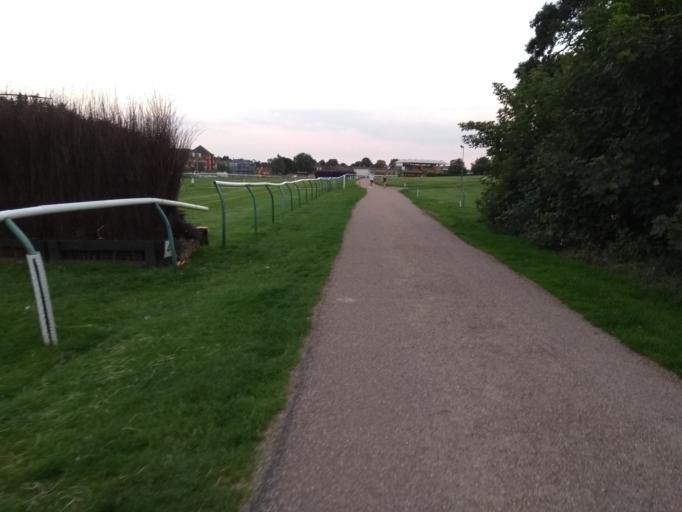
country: GB
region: England
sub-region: Warwickshire
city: Warwick
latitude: 52.2822
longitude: -1.5958
